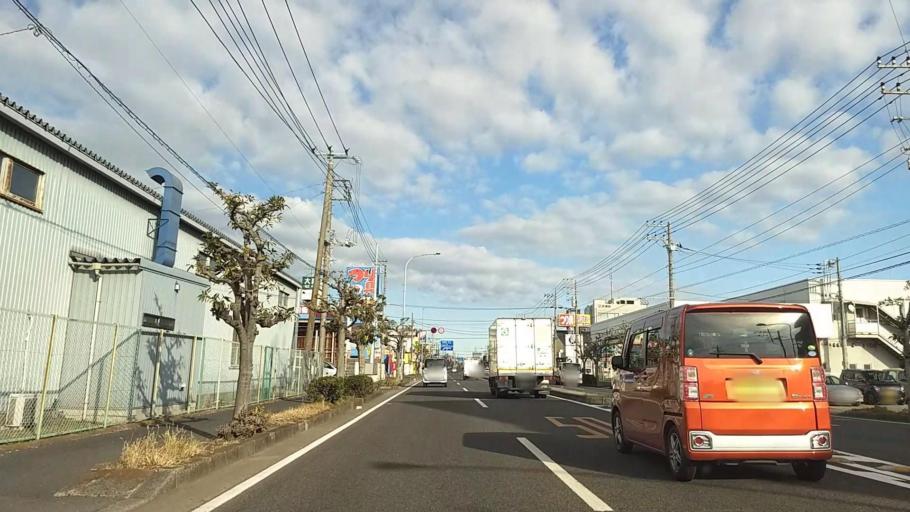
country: JP
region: Kanagawa
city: Hiratsuka
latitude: 35.3437
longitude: 139.3562
